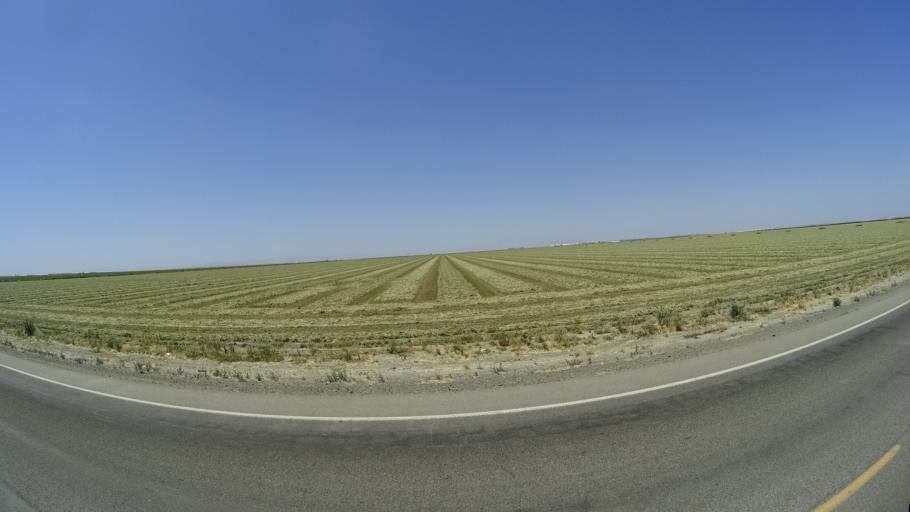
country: US
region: California
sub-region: Kings County
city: Corcoran
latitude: 36.1541
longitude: -119.6458
